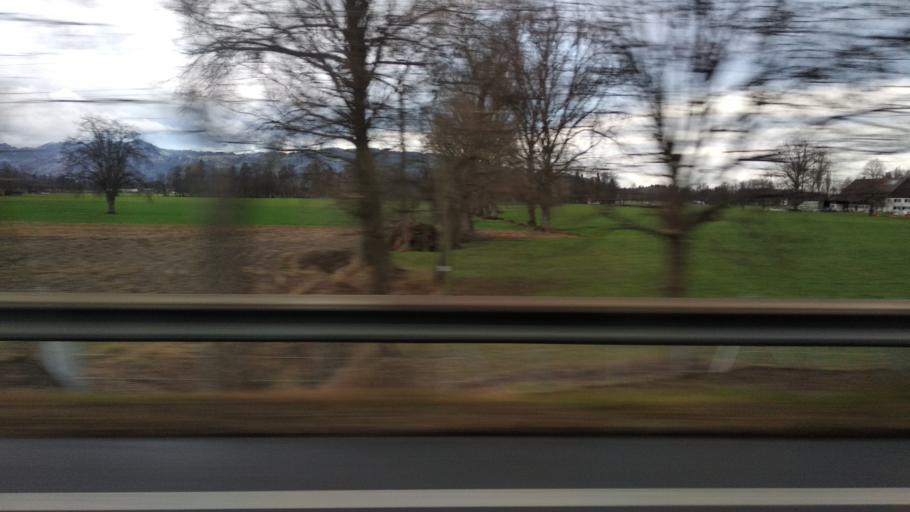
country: AT
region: Vorarlberg
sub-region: Politischer Bezirk Dornbirn
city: Dornbirn
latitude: 47.4103
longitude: 9.7059
